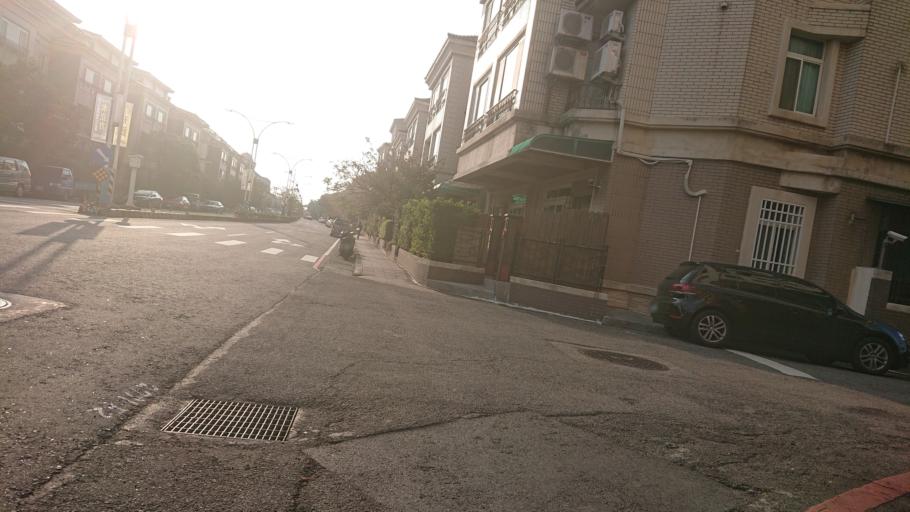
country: TW
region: Taipei
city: Taipei
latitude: 25.1878
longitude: 121.4228
